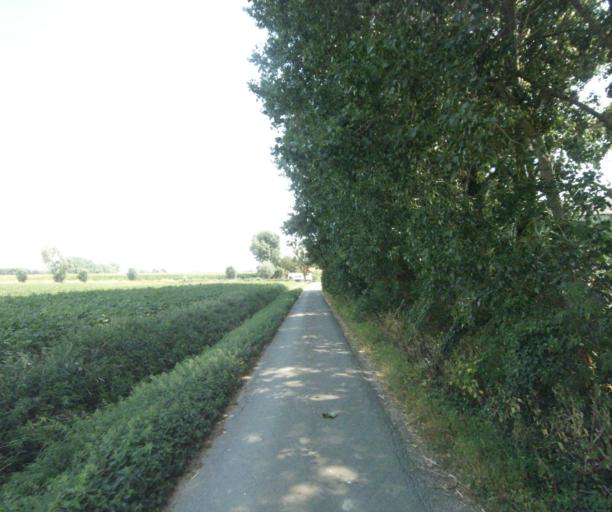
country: FR
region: Nord-Pas-de-Calais
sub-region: Departement du Nord
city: Quesnoy-sur-Deule
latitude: 50.7351
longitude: 3.0003
